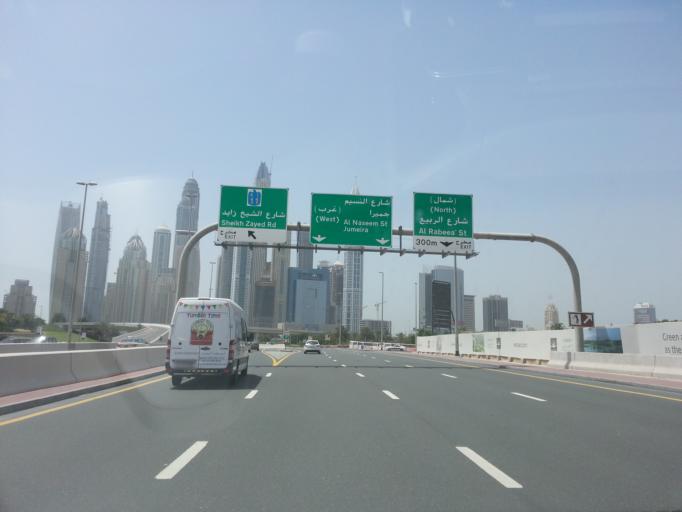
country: AE
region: Dubai
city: Dubai
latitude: 25.0797
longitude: 55.1566
